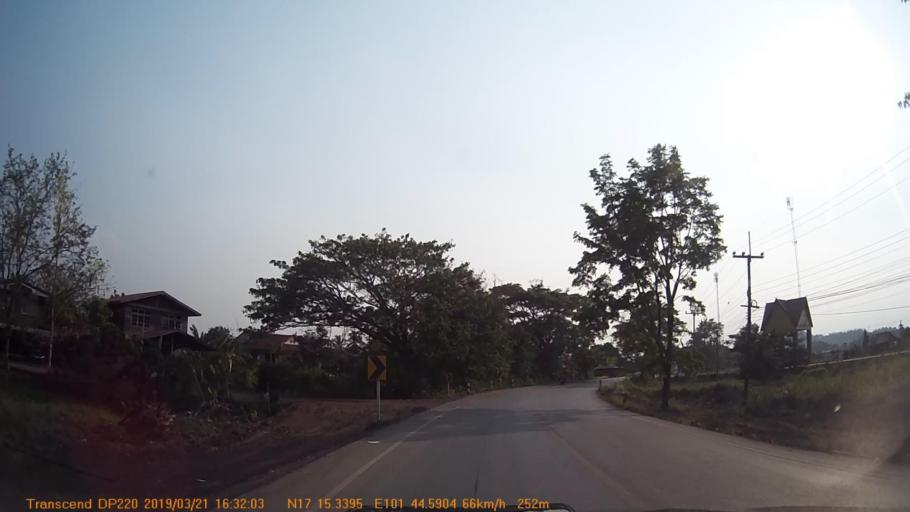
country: TH
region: Loei
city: Wang Saphung
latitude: 17.2555
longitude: 101.7430
